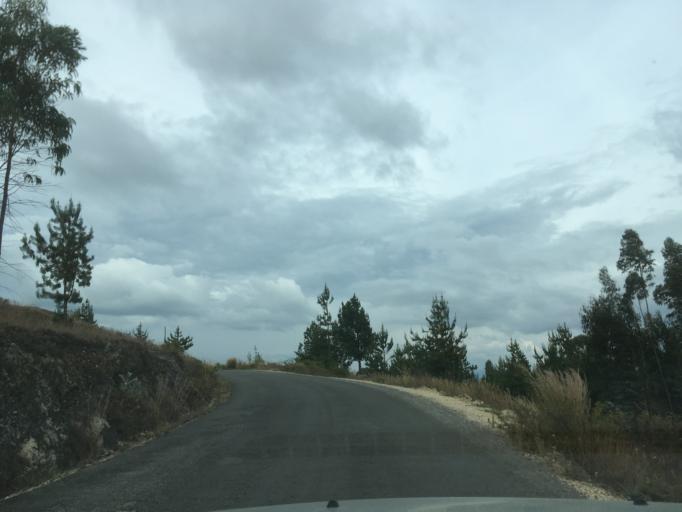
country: CO
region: Boyaca
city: Firavitoba
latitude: 5.6739
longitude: -73.0148
